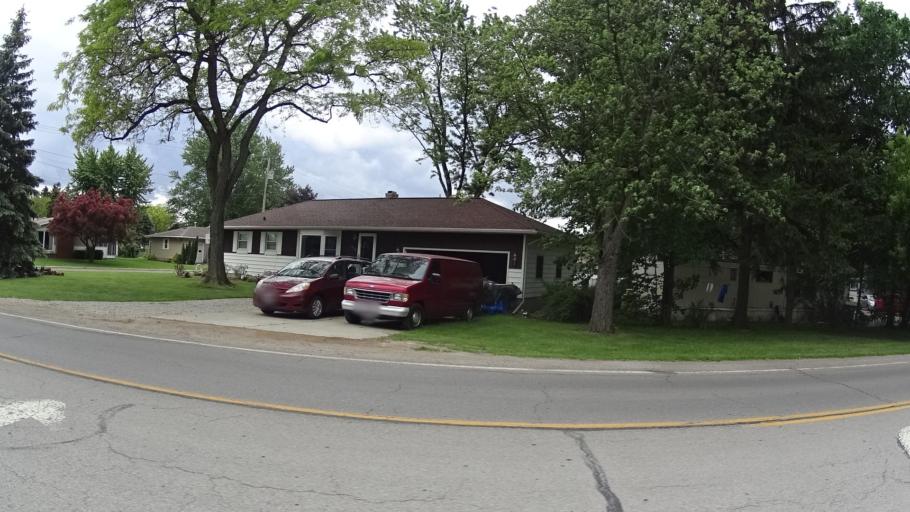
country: US
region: Ohio
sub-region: Erie County
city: Sandusky
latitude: 41.4271
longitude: -82.6946
